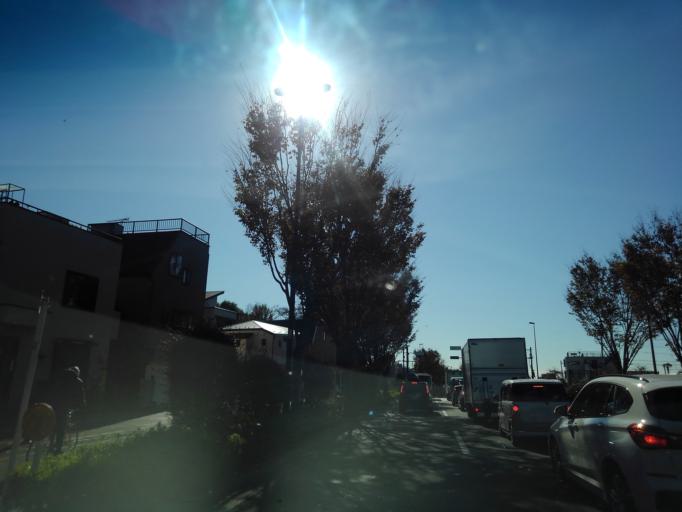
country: JP
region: Tokyo
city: Chofugaoka
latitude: 35.6706
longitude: 139.5446
